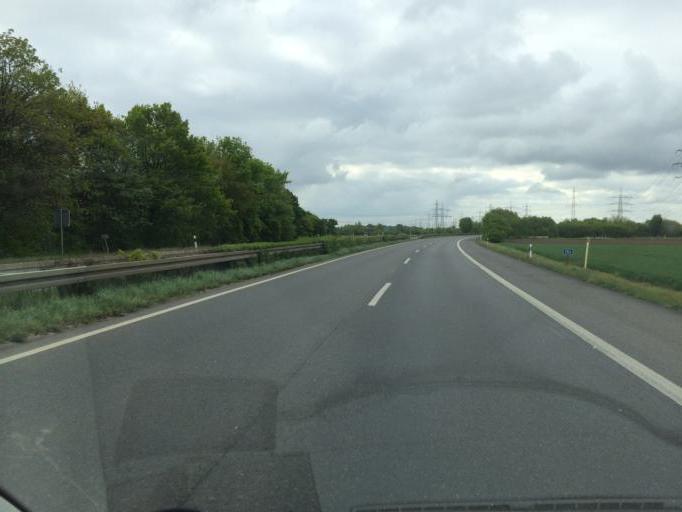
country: DE
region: North Rhine-Westphalia
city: Bruhl
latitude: 50.8466
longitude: 6.9216
